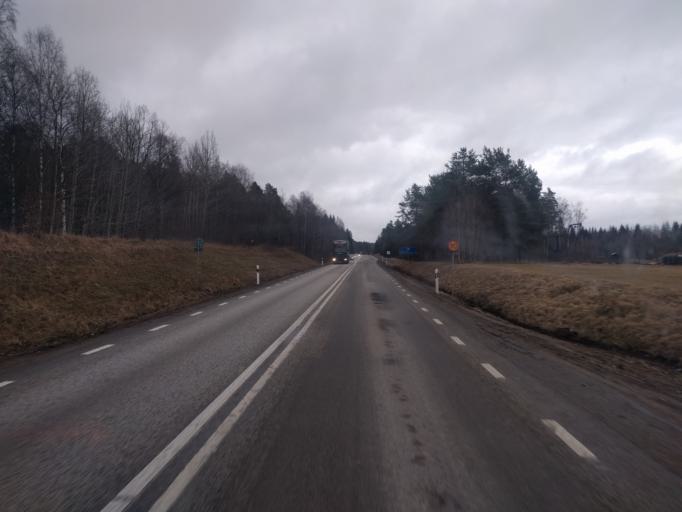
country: SE
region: Joenkoeping
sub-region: Eksjo Kommun
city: Eksjoe
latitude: 57.6621
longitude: 14.9963
